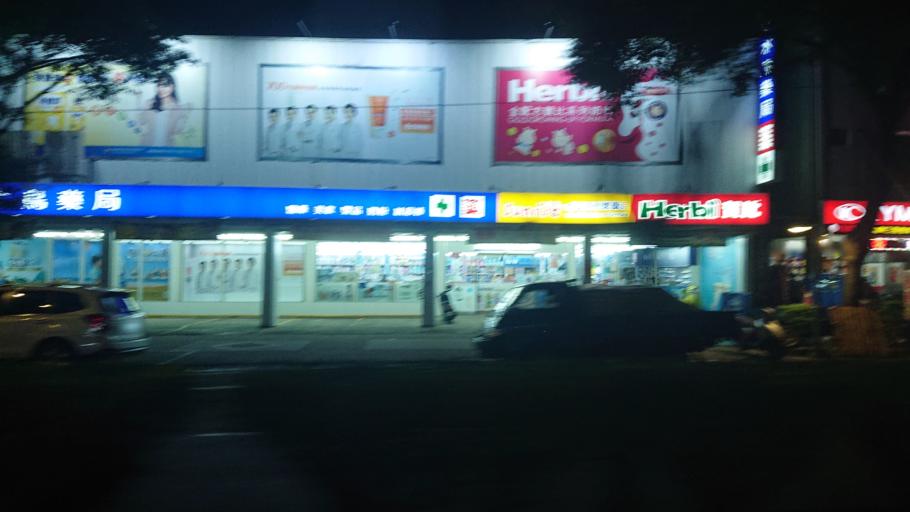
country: TW
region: Taiwan
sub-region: Taoyuan
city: Taoyuan
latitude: 24.9289
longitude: 121.3734
